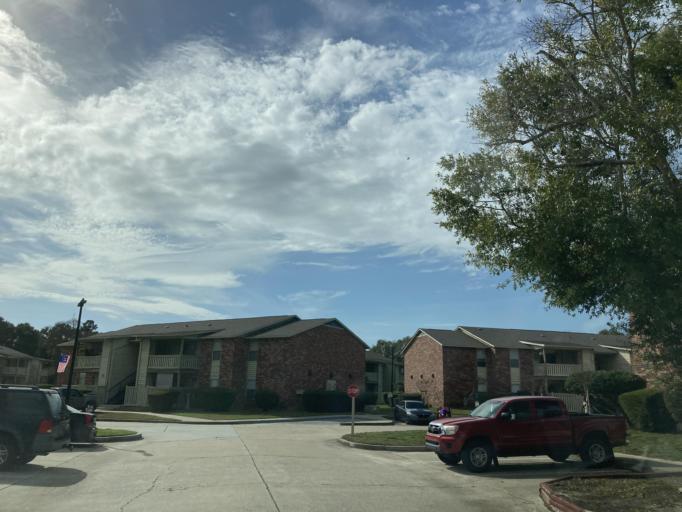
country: US
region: Mississippi
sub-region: Harrison County
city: D'Iberville
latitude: 30.4090
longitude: -88.9733
